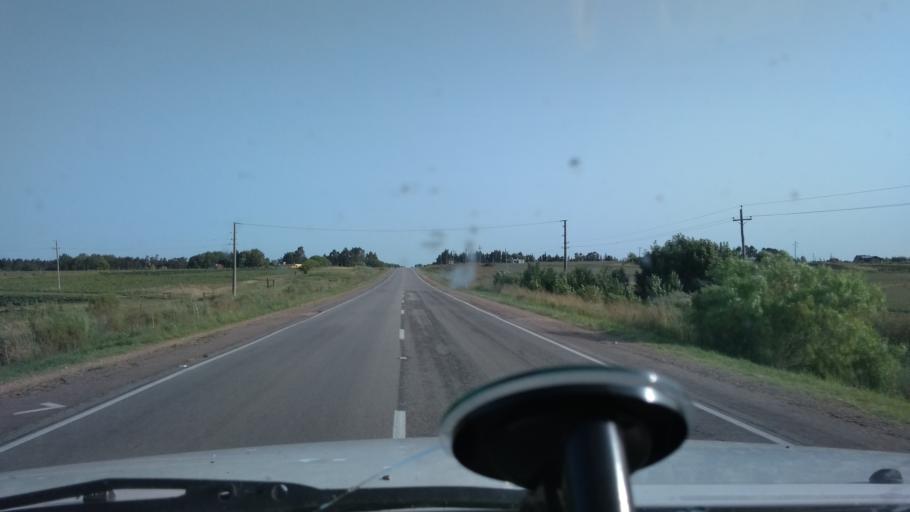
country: UY
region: Canelones
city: Sauce
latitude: -34.5849
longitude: -56.0551
